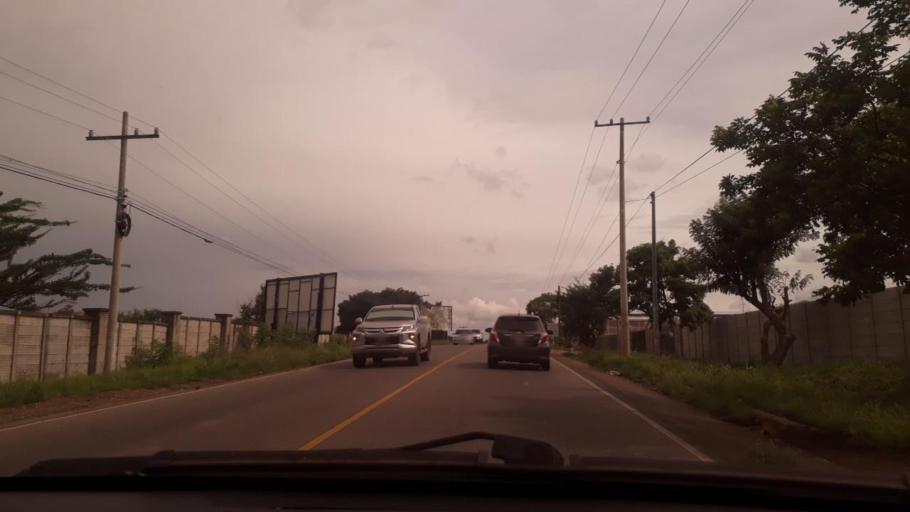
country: GT
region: Jutiapa
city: El Progreso
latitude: 14.3352
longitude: -89.8561
